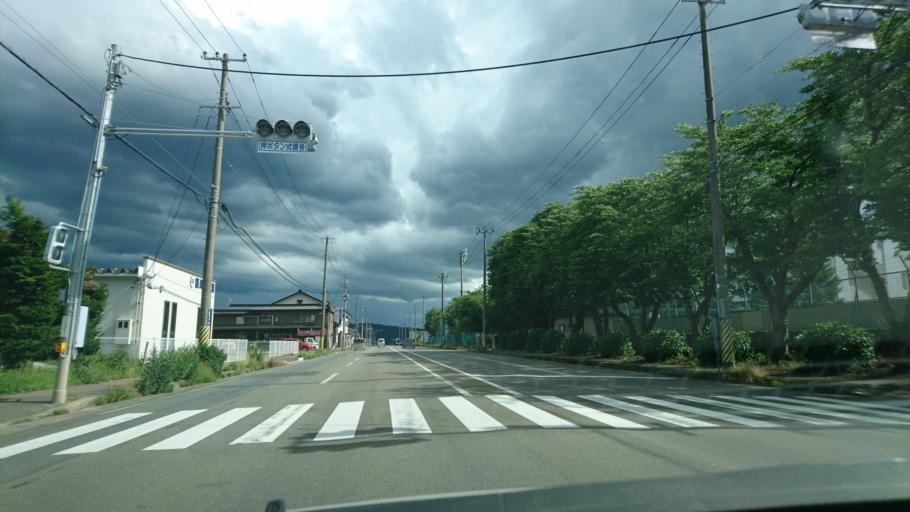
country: JP
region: Iwate
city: Kitakami
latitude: 39.3035
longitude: 141.1283
